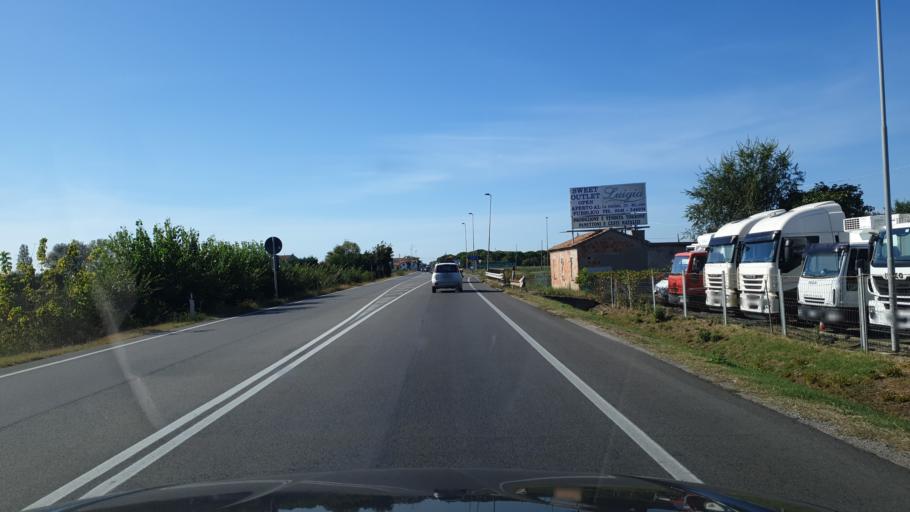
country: IT
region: Emilia-Romagna
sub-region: Provincia di Rimini
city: Santa Giustina
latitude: 44.0955
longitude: 12.5037
